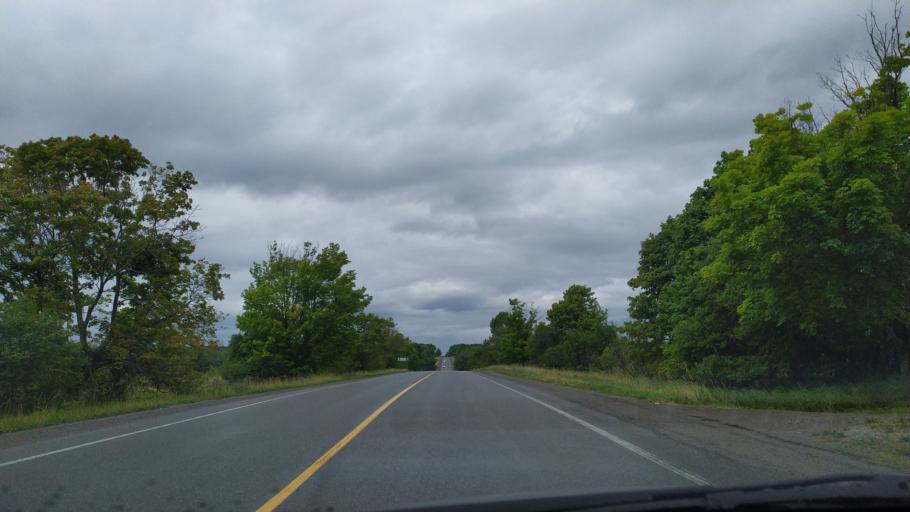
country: CA
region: Ontario
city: Quinte West
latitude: 43.9641
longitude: -77.4999
